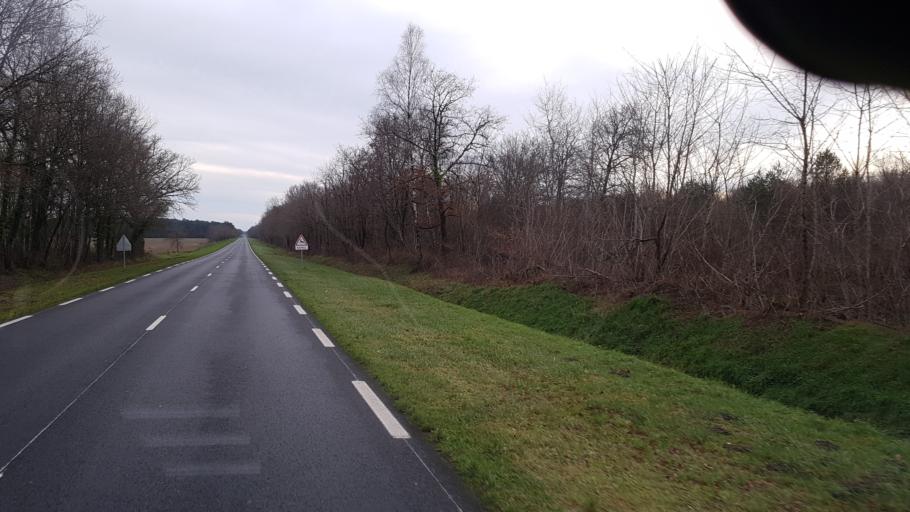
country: FR
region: Centre
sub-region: Departement du Loir-et-Cher
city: Nouan-le-Fuzelier
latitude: 47.4986
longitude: 2.0376
